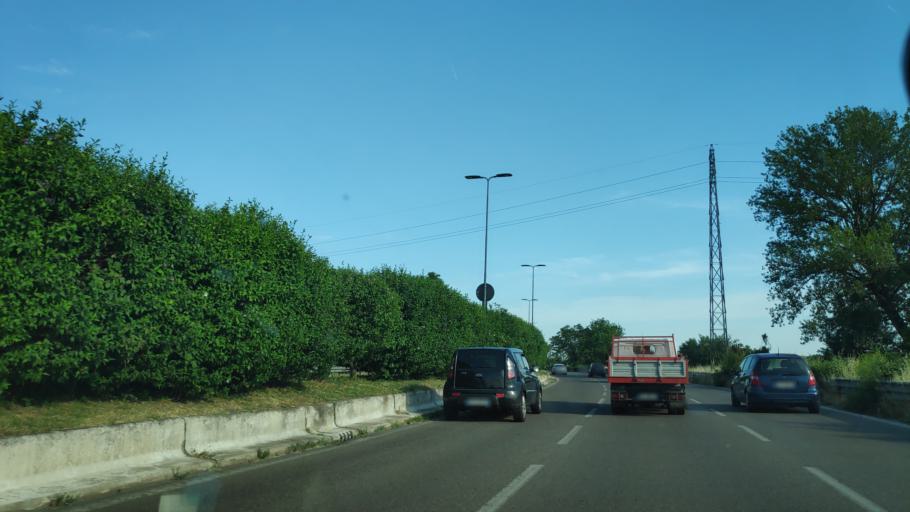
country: IT
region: Lombardy
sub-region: Citta metropolitana di Milano
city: Noverasco-Sporting Mirasole
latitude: 45.4240
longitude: 9.1976
